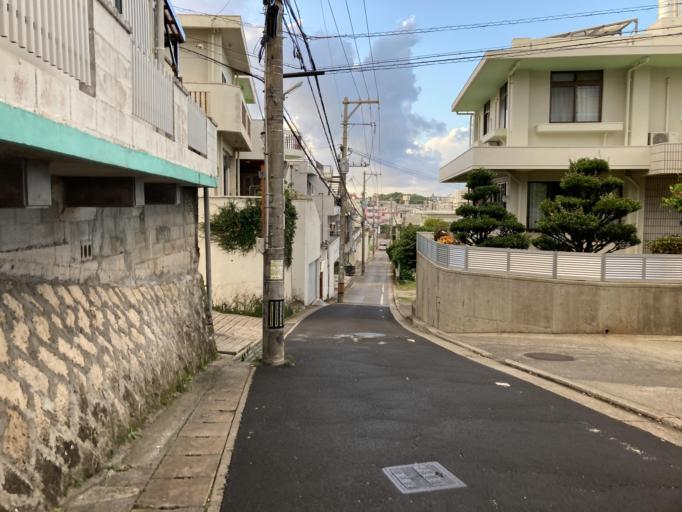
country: JP
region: Okinawa
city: Naha-shi
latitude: 26.2242
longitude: 127.7226
